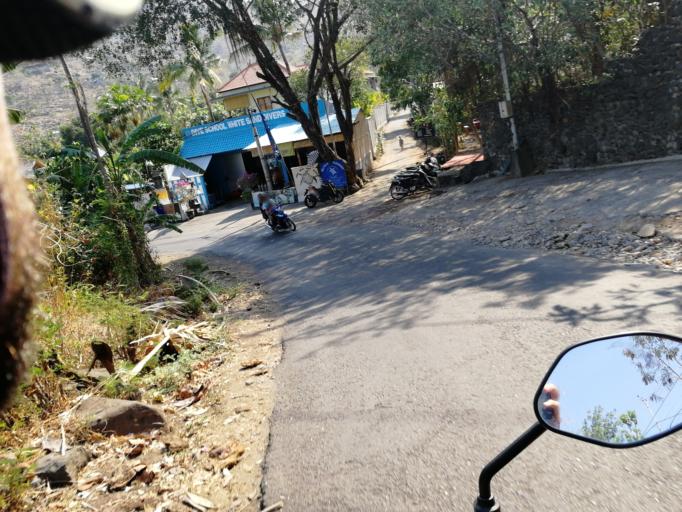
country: ID
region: Bali
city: Biaslantang Kaler
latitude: -8.3479
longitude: 115.6805
